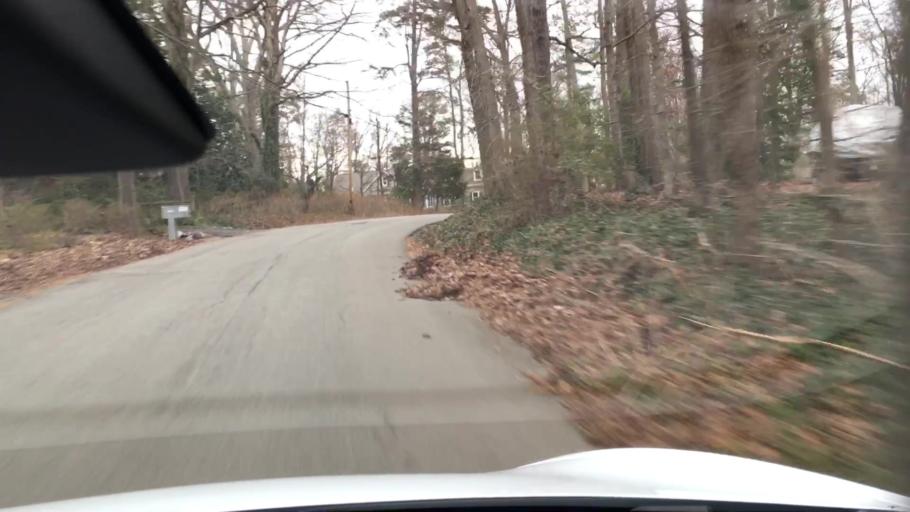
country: US
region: Virginia
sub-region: Chesterfield County
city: Bon Air
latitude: 37.5301
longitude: -77.5679
